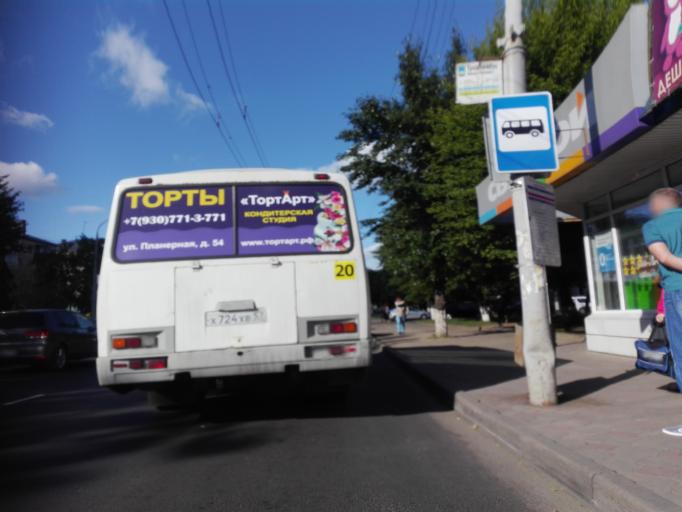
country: RU
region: Orjol
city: Orel
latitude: 52.9794
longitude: 36.1052
